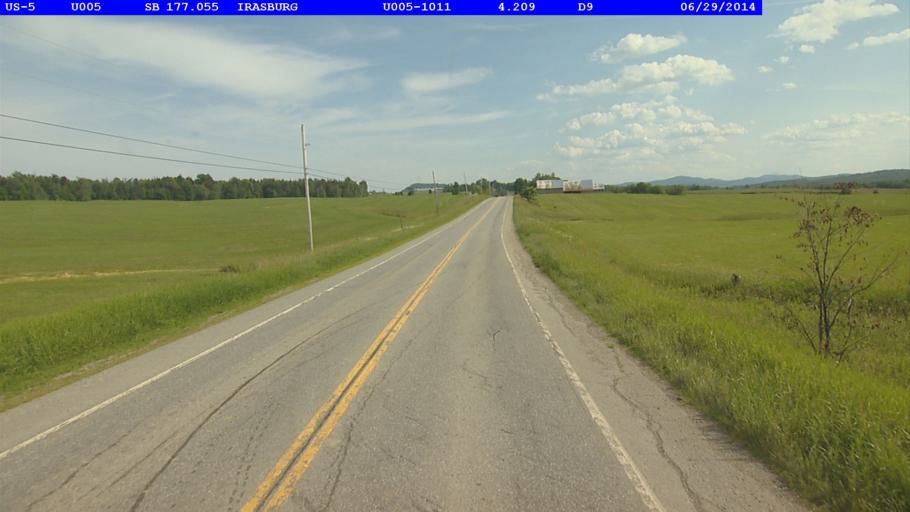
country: US
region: Vermont
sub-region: Orleans County
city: Newport
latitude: 44.8524
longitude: -72.2636
